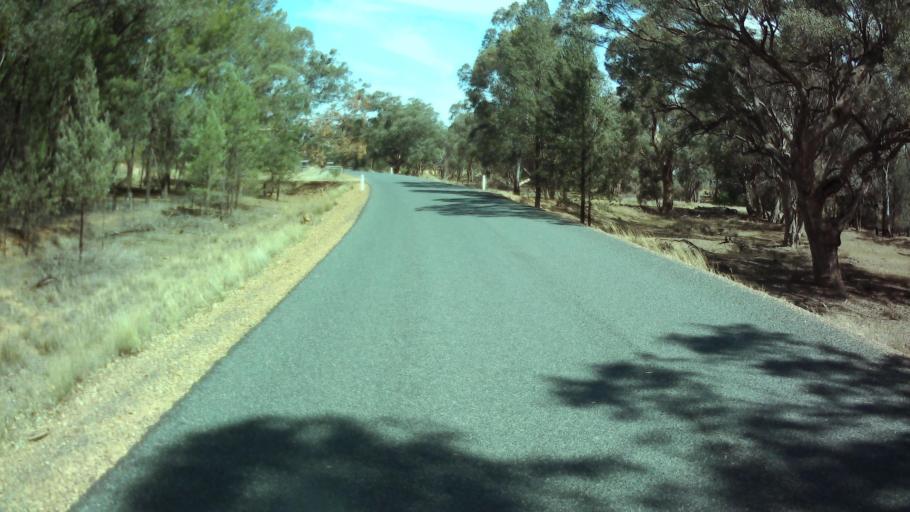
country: AU
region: New South Wales
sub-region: Weddin
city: Grenfell
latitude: -34.0787
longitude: 148.1457
